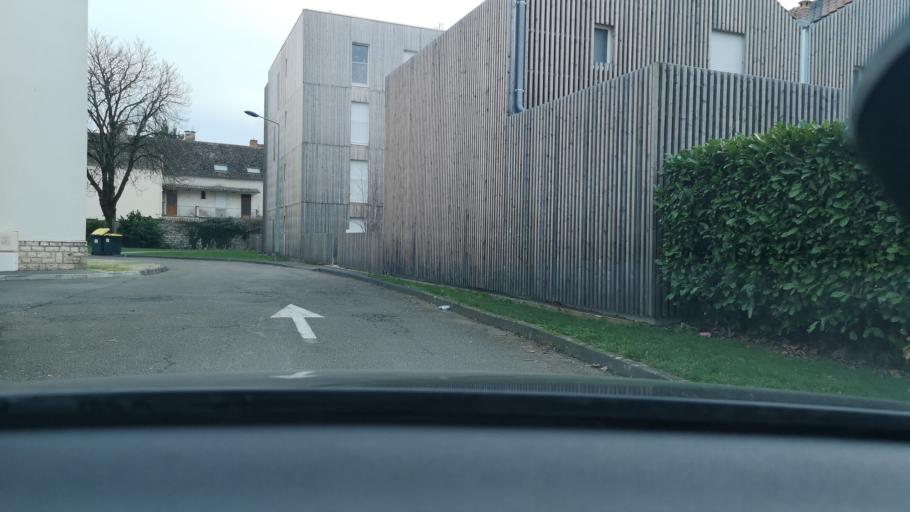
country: FR
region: Bourgogne
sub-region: Departement de Saone-et-Loire
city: Chalon-sur-Saone
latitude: 46.7803
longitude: 4.8371
